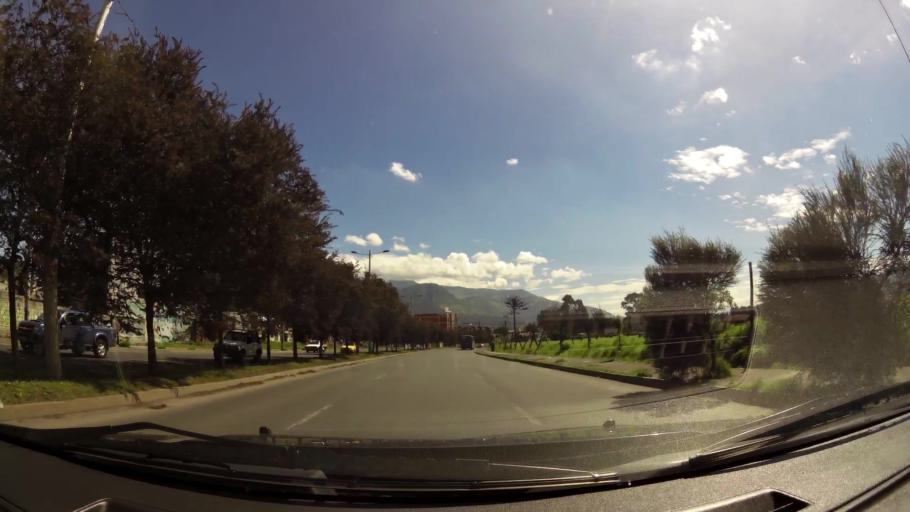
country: EC
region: Pichincha
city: Quito
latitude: -0.2939
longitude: -78.5587
